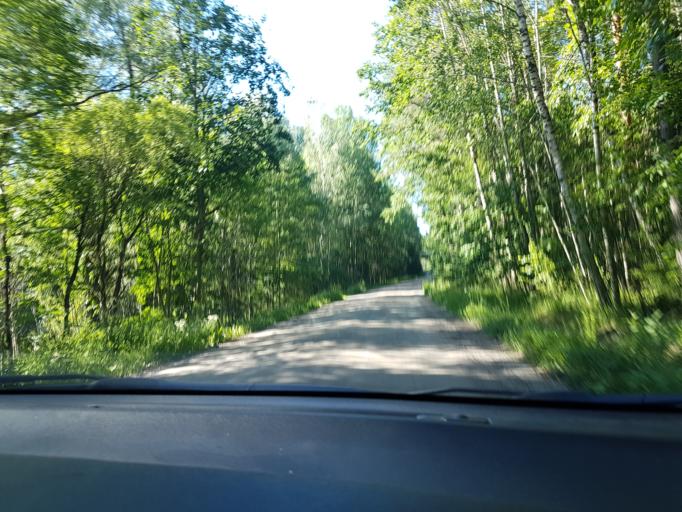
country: FI
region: Uusimaa
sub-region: Helsinki
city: Sibbo
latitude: 60.2745
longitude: 25.2343
